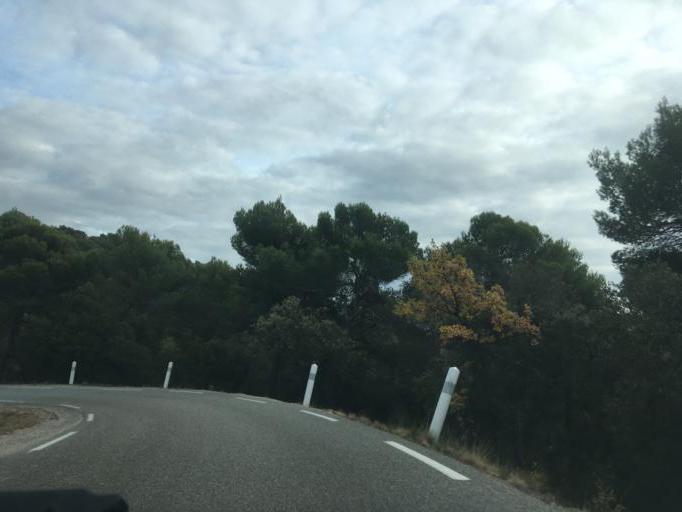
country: FR
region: Provence-Alpes-Cote d'Azur
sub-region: Departement du Var
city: Villecroze
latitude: 43.5835
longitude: 6.3085
